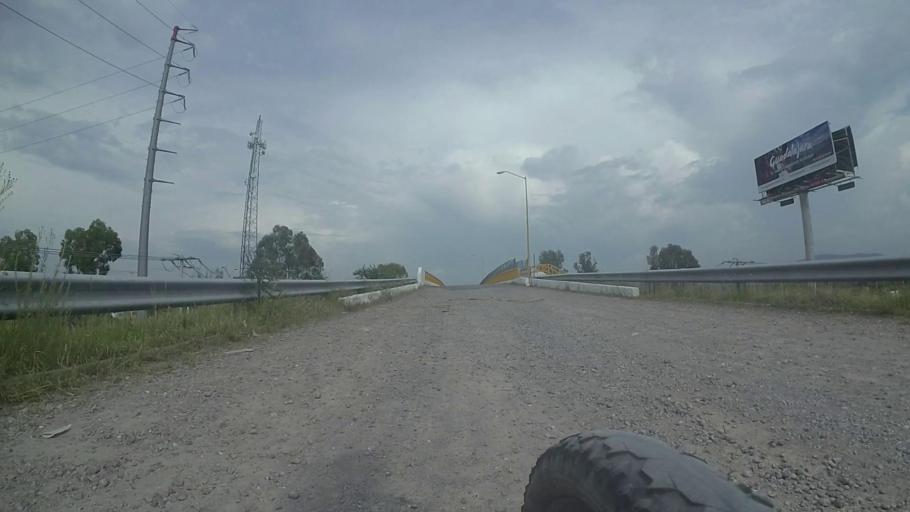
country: MX
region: Aguascalientes
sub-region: Aguascalientes
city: Penuelas (El Cienegal)
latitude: 21.7265
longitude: -102.2774
